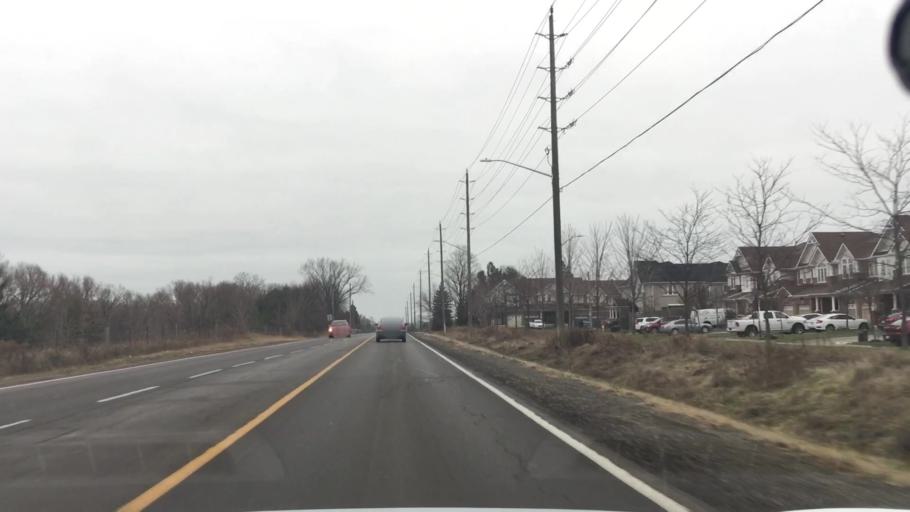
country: CA
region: Ontario
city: Oshawa
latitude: 43.9389
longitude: -78.8276
